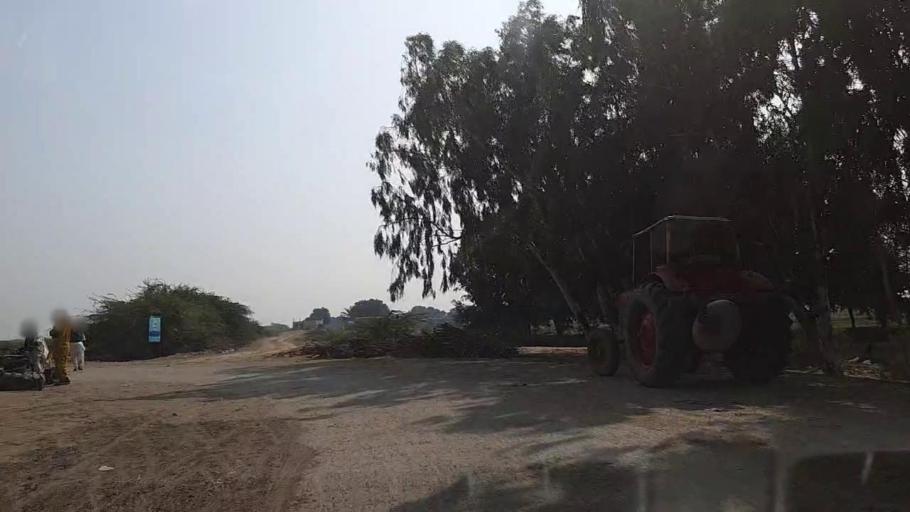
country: PK
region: Sindh
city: Keti Bandar
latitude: 24.2235
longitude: 67.6664
